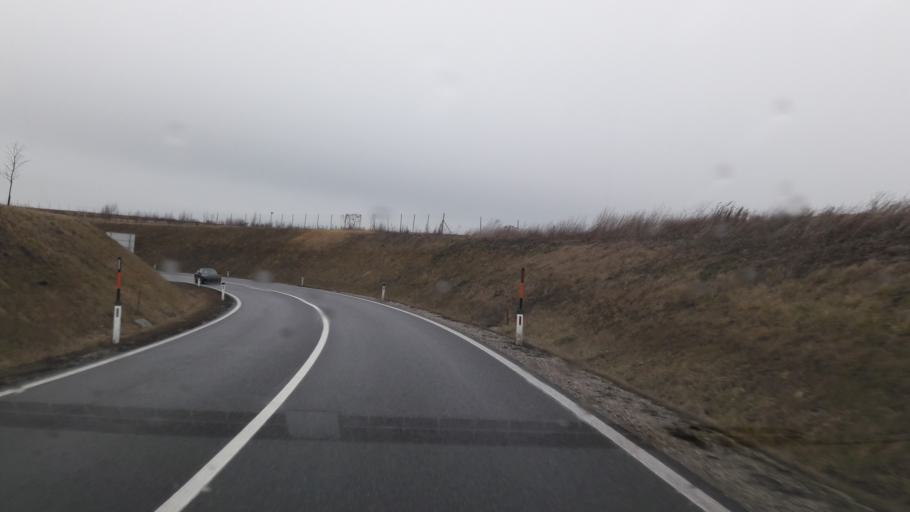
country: AT
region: Lower Austria
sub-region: Politischer Bezirk Mistelbach
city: Hochleithen
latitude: 48.4282
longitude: 16.5517
